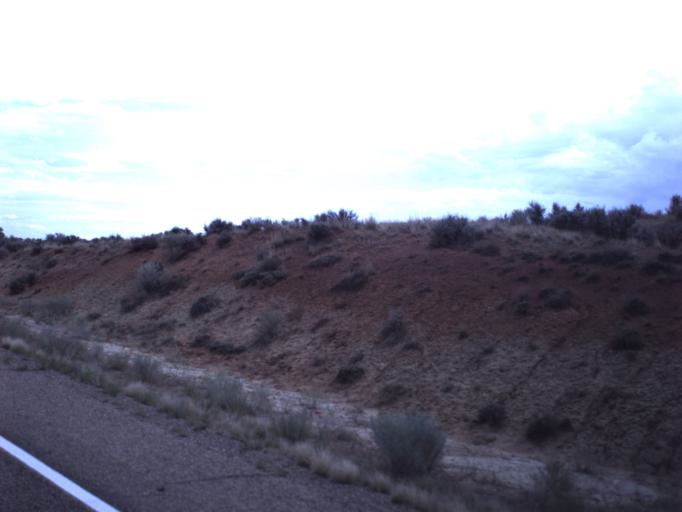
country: US
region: Utah
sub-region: Uintah County
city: Naples
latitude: 40.1577
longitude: -109.3072
